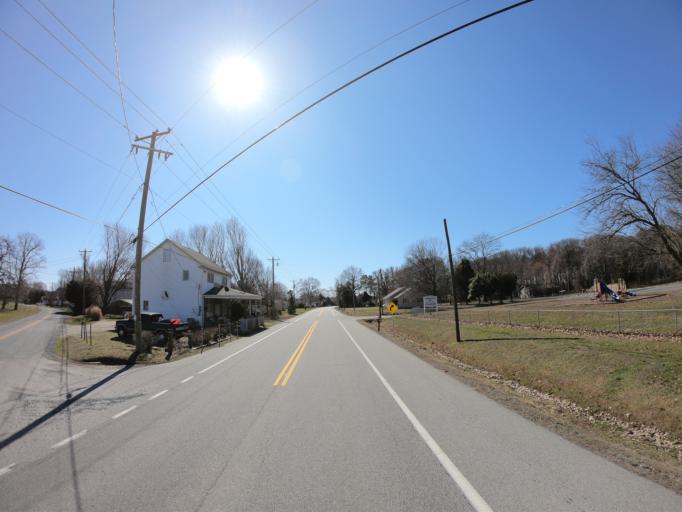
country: US
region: Maryland
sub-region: Kent County
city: Rock Hall
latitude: 39.1555
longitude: -76.2076
